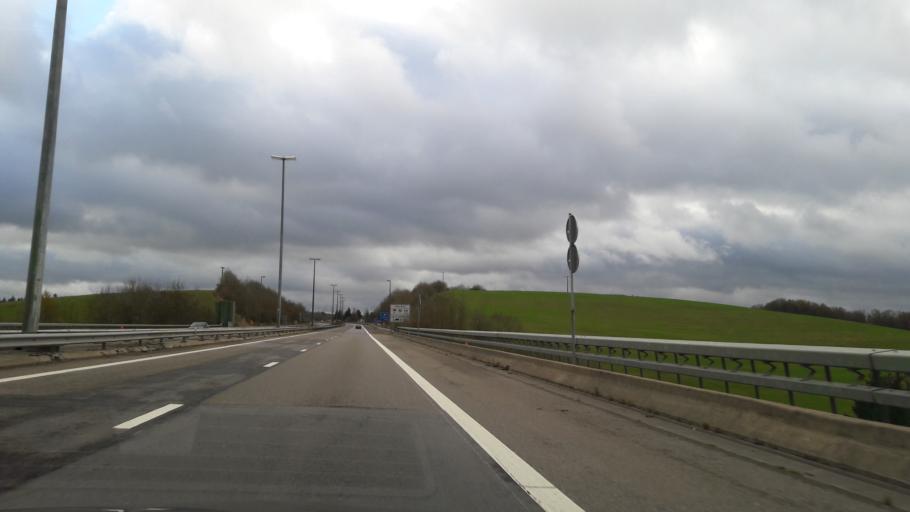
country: DE
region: Rheinland-Pfalz
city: Winterspelt
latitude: 50.2362
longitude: 6.1818
